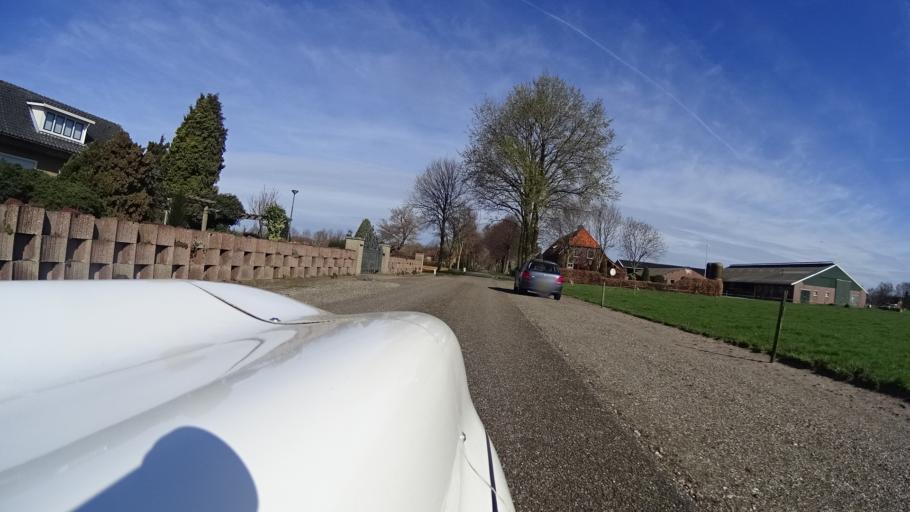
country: NL
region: North Brabant
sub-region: Gemeente Mill en Sint Hubert
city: Wilbertoord
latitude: 51.6829
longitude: 5.7511
